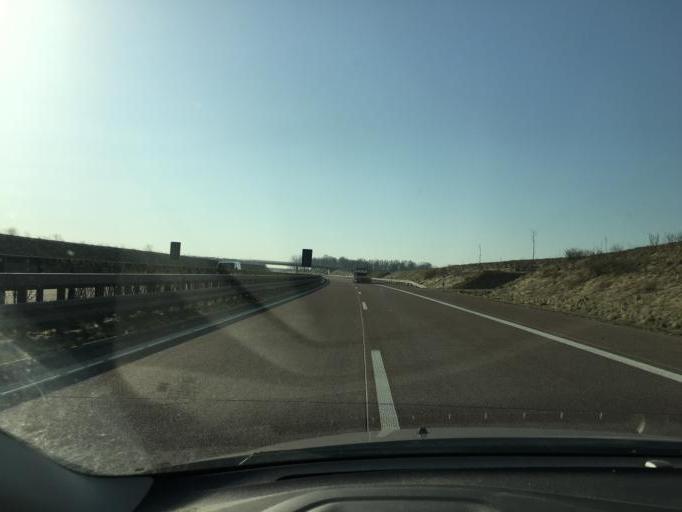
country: DE
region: Saxony
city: Penig
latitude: 50.9159
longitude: 12.6981
